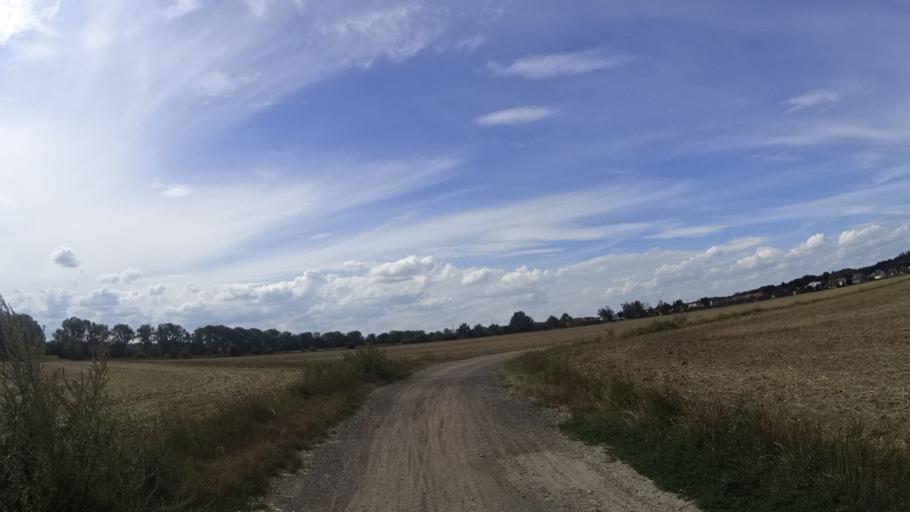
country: CZ
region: Olomoucky
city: Skrben
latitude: 49.6639
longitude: 17.1788
